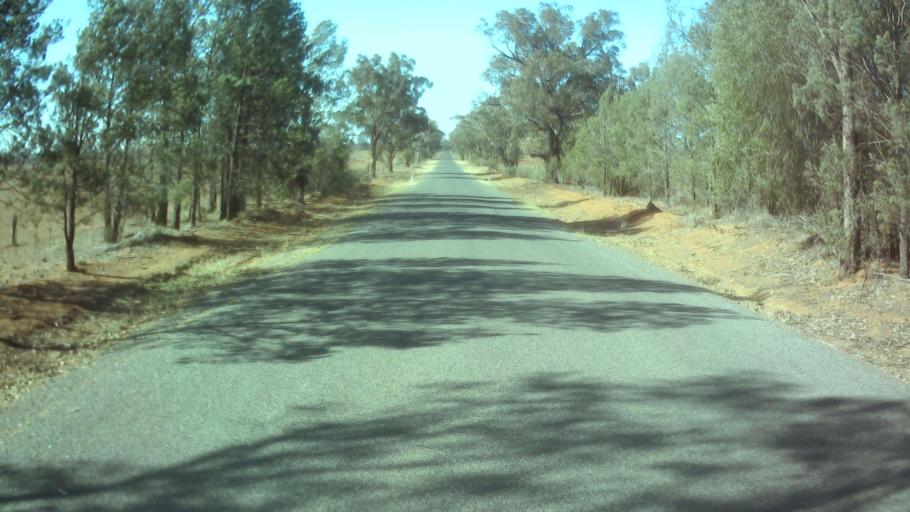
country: AU
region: New South Wales
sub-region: Forbes
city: Forbes
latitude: -33.7028
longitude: 147.8063
